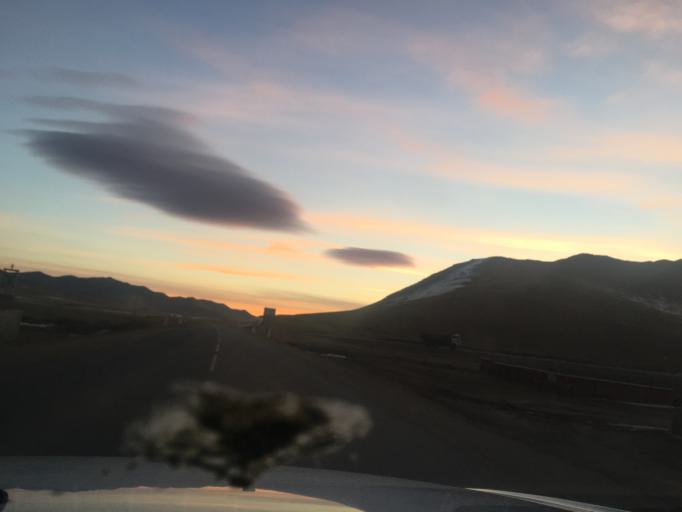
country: MN
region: Central Aimak
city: Mandal
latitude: 48.1202
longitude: 106.6483
